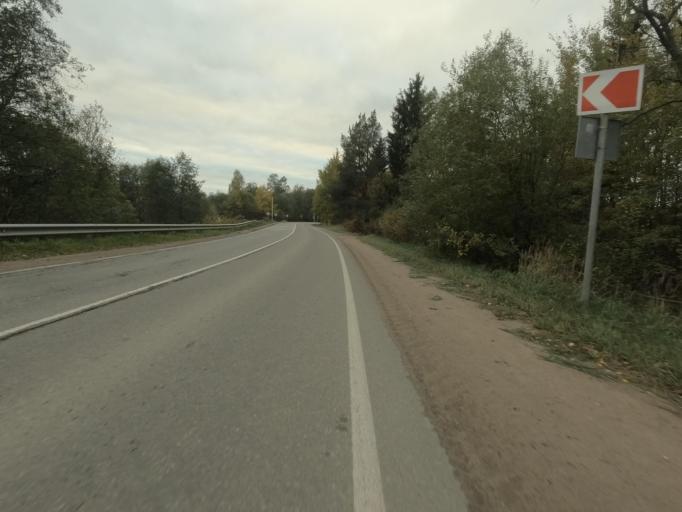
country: RU
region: Leningrad
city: Pavlovo
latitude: 59.7864
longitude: 30.9681
